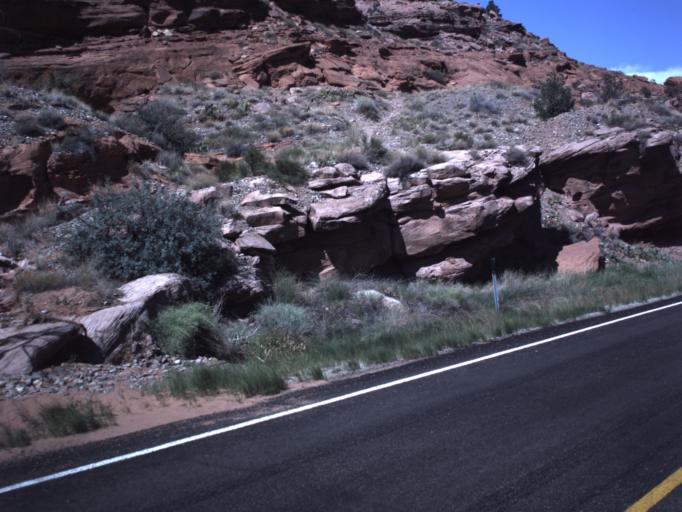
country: US
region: Utah
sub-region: Grand County
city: Moab
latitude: 38.5610
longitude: -109.5855
